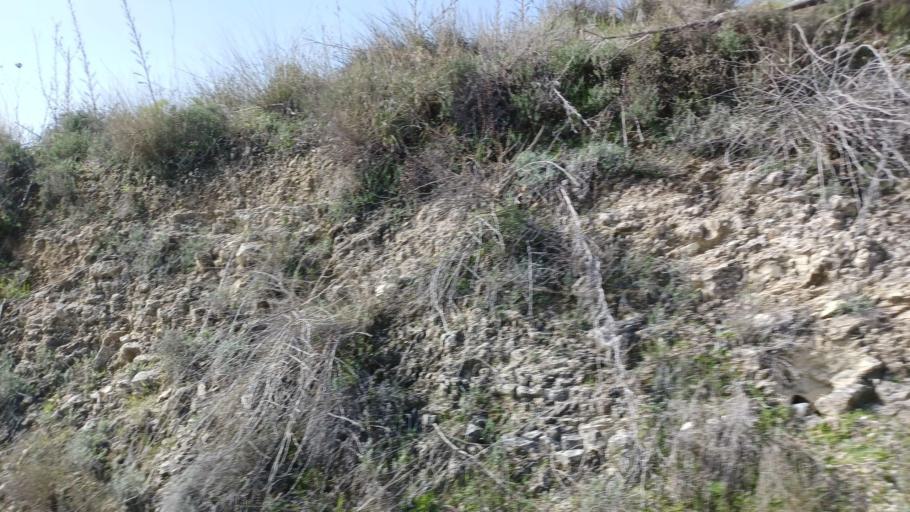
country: CY
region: Limassol
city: Pachna
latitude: 34.7973
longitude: 32.6946
